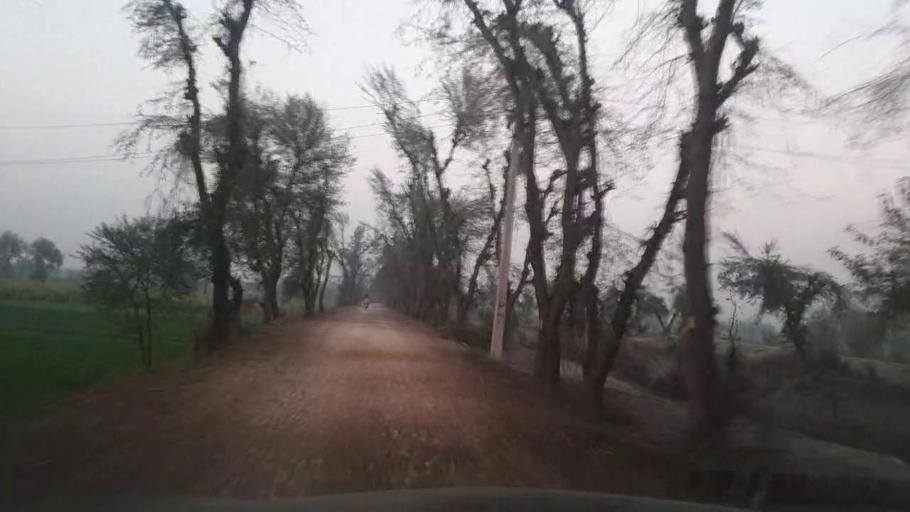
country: PK
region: Sindh
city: Ubauro
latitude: 28.1797
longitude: 69.7801
